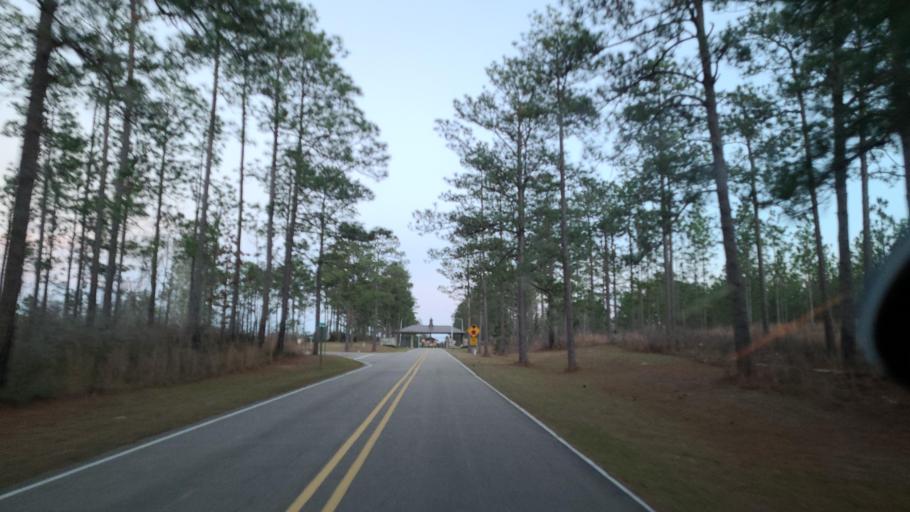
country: US
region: Mississippi
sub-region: Forrest County
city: Hattiesburg
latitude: 31.2096
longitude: -89.2453
